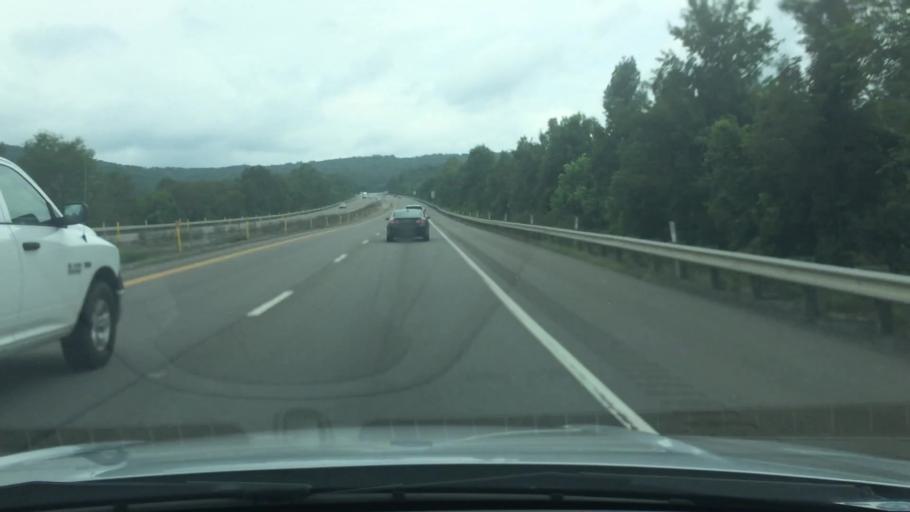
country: US
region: Tennessee
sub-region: Campbell County
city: Jacksboro
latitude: 36.4185
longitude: -84.2839
